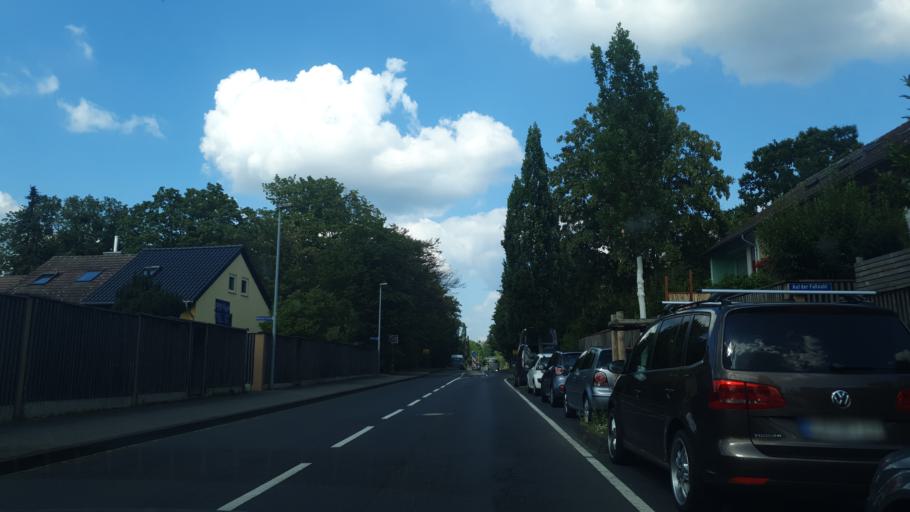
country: DE
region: Rheinland-Pfalz
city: Koblenz
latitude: 50.3424
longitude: 7.6139
